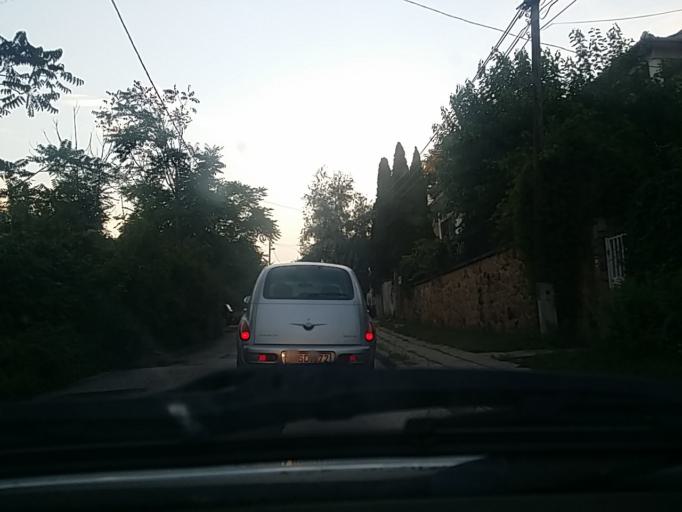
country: HU
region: Budapest
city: Budapest II. keruelet
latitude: 47.5326
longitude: 19.0217
